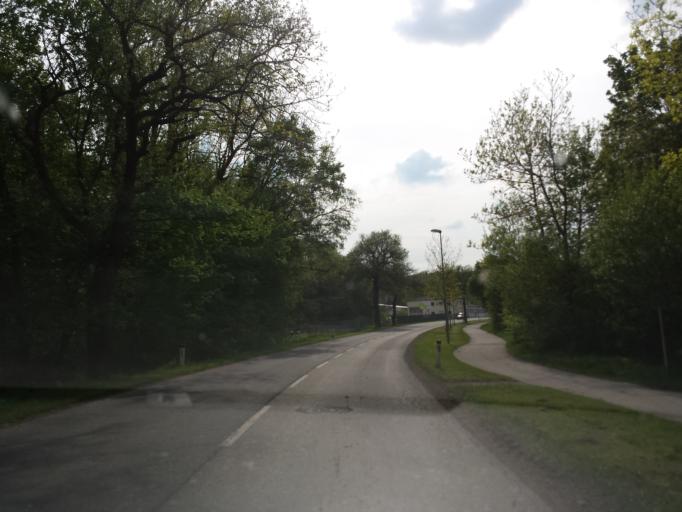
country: AT
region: Lower Austria
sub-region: Politischer Bezirk Modling
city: Kaltenleutgeben
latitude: 48.1344
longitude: 16.1865
